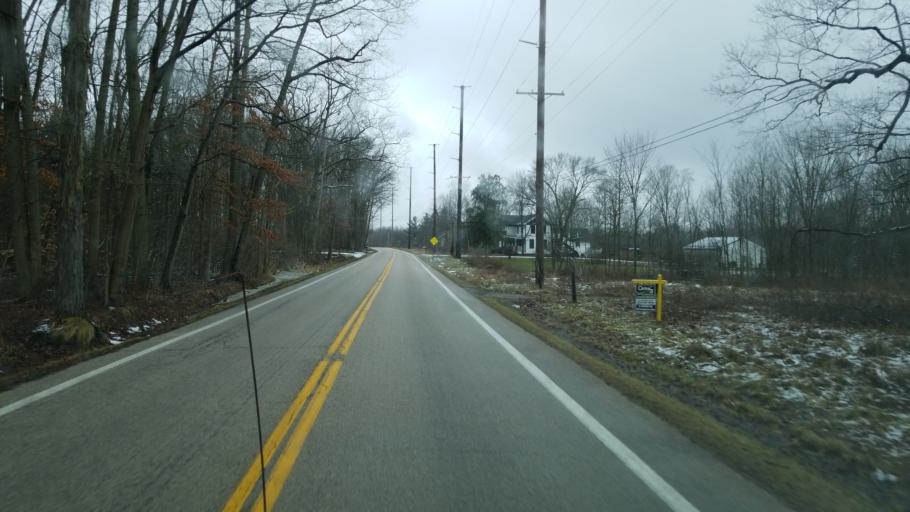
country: US
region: Ohio
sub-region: Portage County
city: Windham
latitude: 41.3097
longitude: -81.0003
